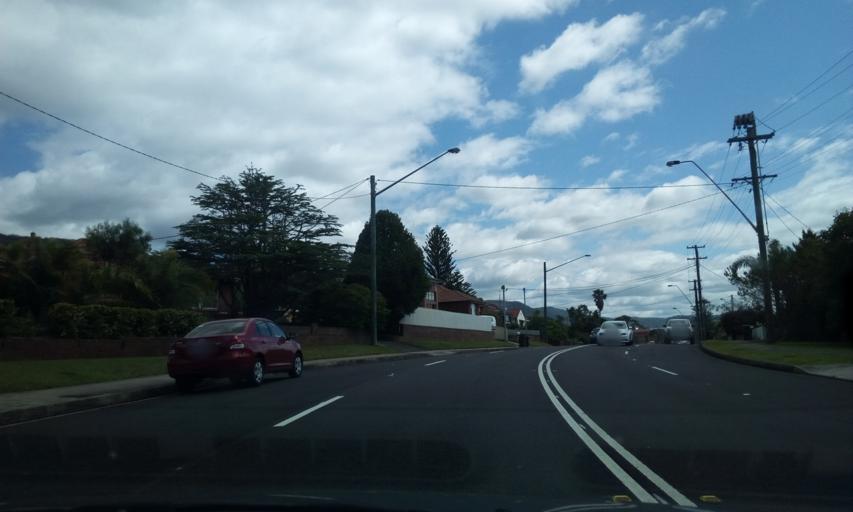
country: AU
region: New South Wales
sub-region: Wollongong
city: Corrimal
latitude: -34.3781
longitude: 150.8962
